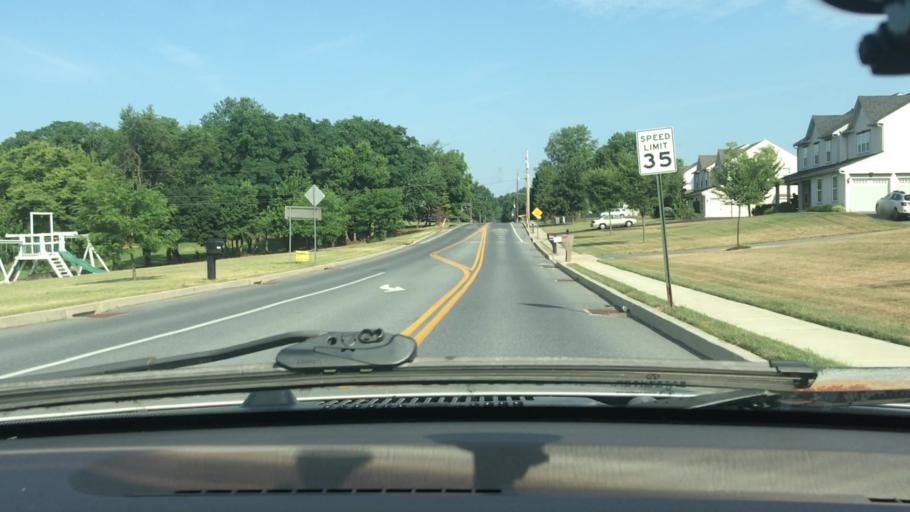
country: US
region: Pennsylvania
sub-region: Lancaster County
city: Rheems
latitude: 40.1424
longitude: -76.5670
